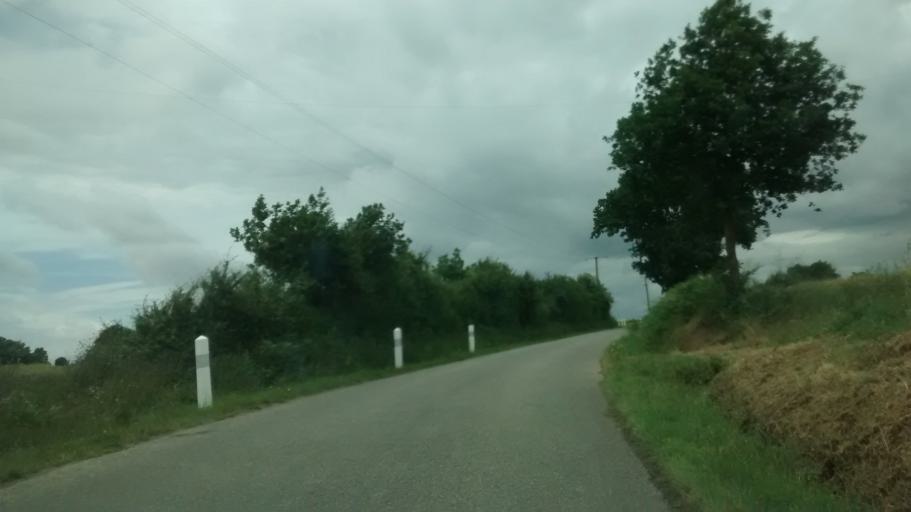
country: FR
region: Brittany
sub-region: Departement du Morbihan
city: Carentoir
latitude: 47.8029
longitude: -2.1155
